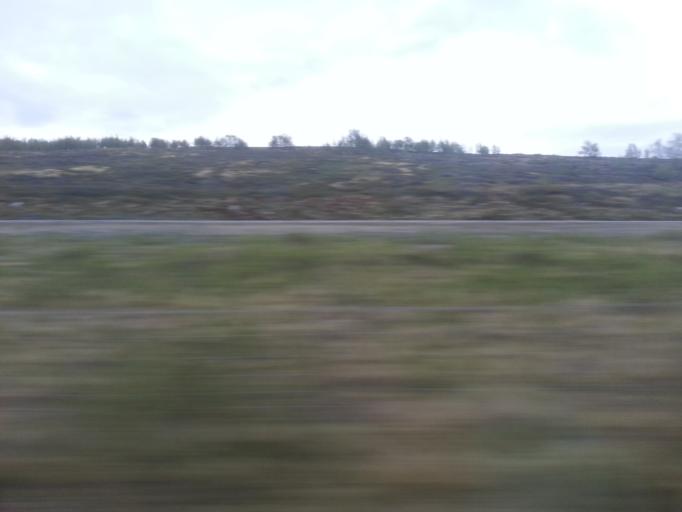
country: NO
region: Oppland
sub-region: Dovre
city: Dovre
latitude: 62.2367
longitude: 9.5291
